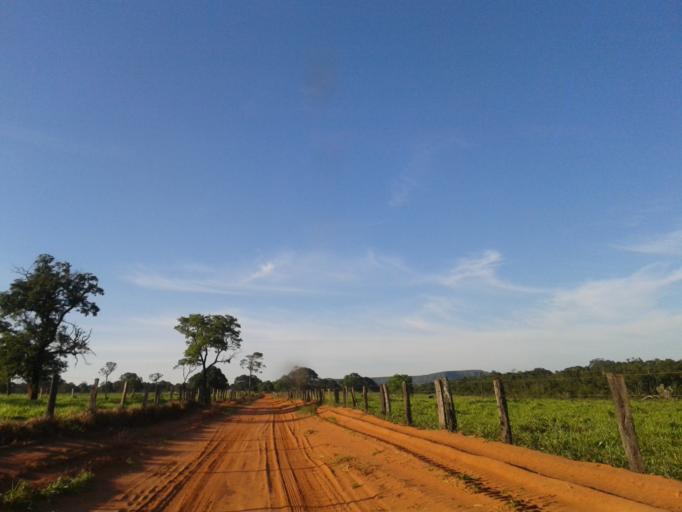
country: BR
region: Minas Gerais
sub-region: Santa Vitoria
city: Santa Vitoria
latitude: -18.9408
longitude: -49.8603
